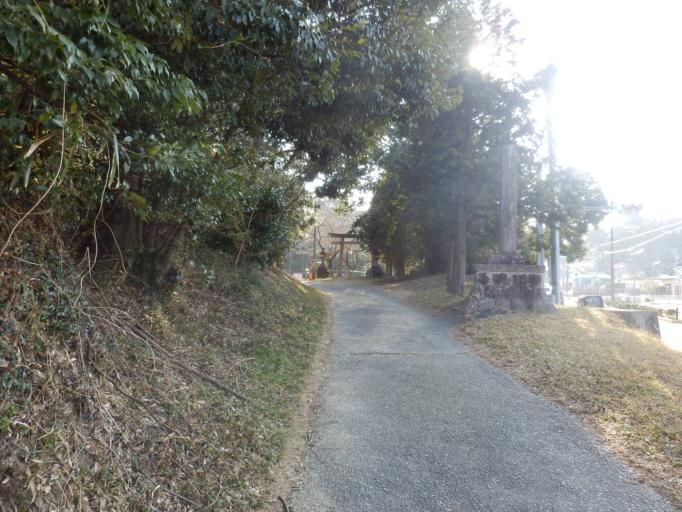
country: JP
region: Shizuoka
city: Kosai-shi
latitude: 34.7145
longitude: 137.5337
